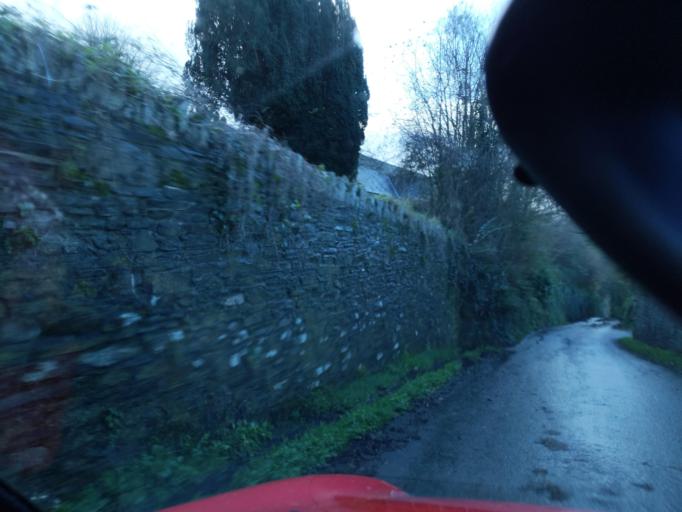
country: GB
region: England
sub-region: Cornwall
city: Looe
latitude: 50.3379
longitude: -4.4900
